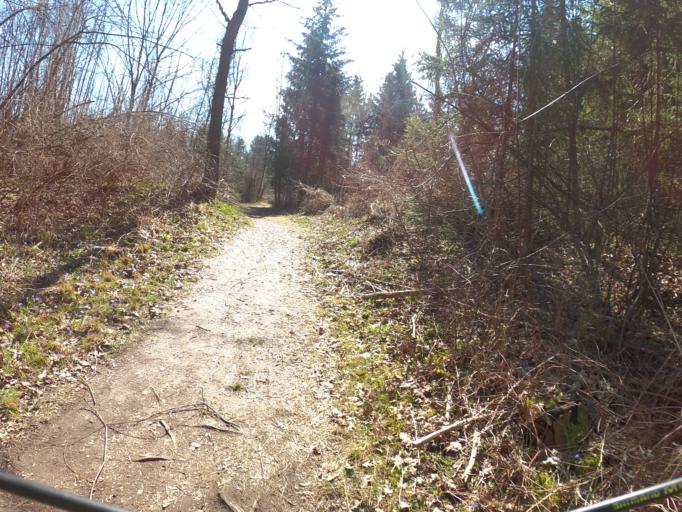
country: DE
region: Bavaria
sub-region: Swabia
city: Nersingen
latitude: 48.4423
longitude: 10.1341
